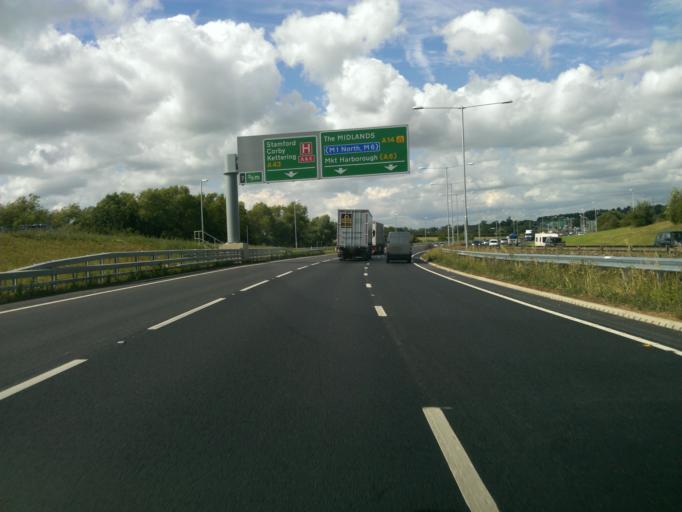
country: GB
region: England
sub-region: Northamptonshire
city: Kettering
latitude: 52.3909
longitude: -0.7494
